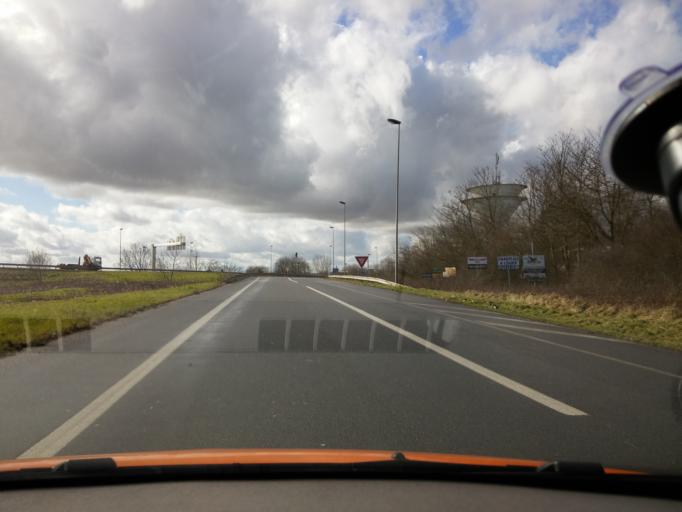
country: FR
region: Ile-de-France
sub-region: Departement de l'Essonne
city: Villejust
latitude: 48.6869
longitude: 2.2146
